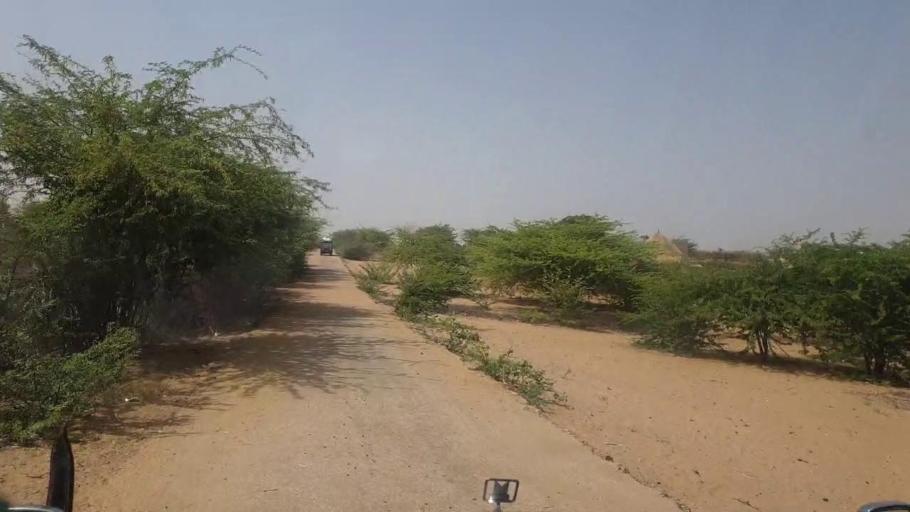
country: PK
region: Sindh
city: Islamkot
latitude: 25.1505
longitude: 70.2064
